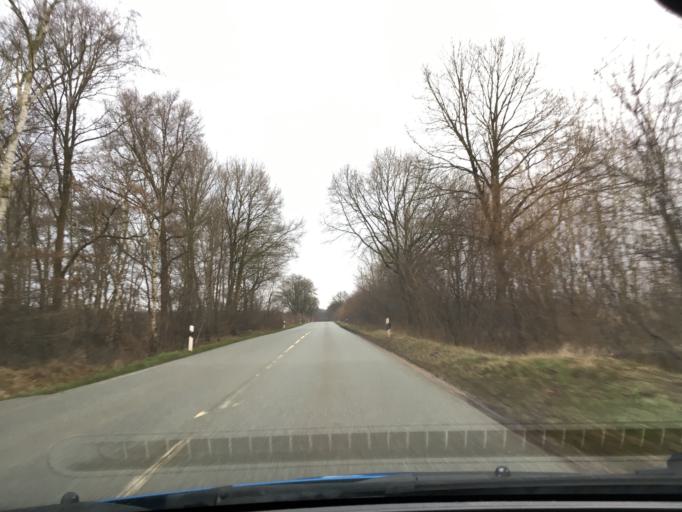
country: DE
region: Schleswig-Holstein
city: Siebeneichen
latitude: 53.5166
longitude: 10.6153
